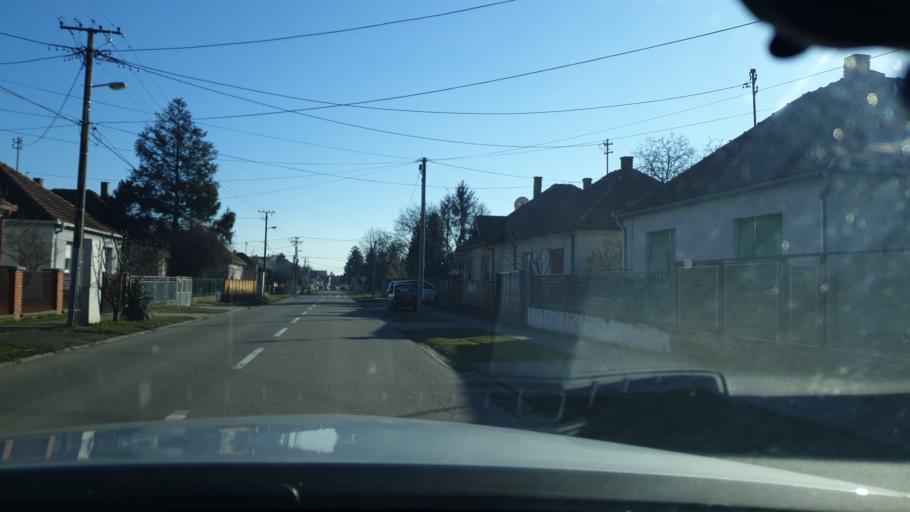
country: RS
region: Autonomna Pokrajina Vojvodina
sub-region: Sremski Okrug
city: Ruma
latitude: 45.0174
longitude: 19.8167
